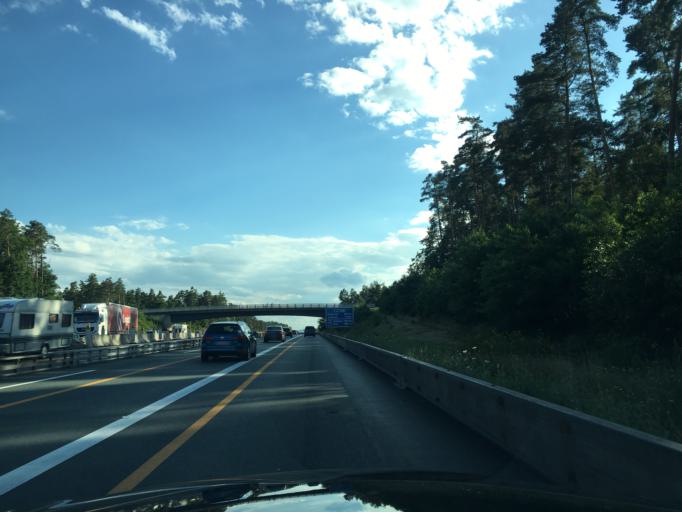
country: DE
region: Bavaria
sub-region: Regierungsbezirk Mittelfranken
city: Wendelstein
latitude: 49.3695
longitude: 11.1250
